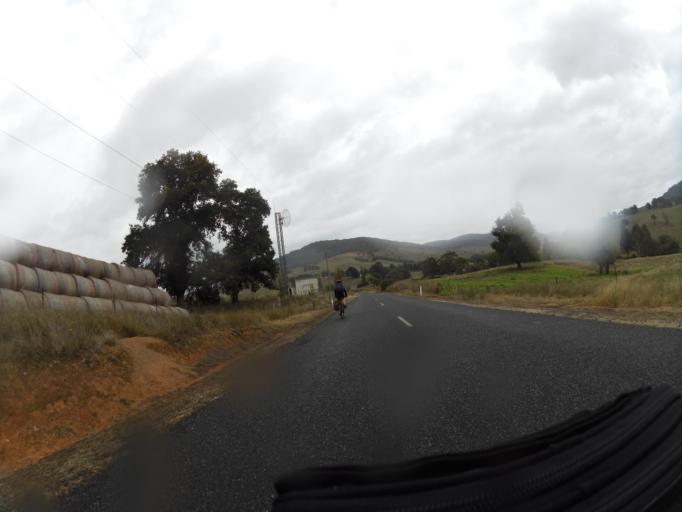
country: AU
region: New South Wales
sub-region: Greater Hume Shire
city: Holbrook
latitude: -36.2368
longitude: 147.6474
